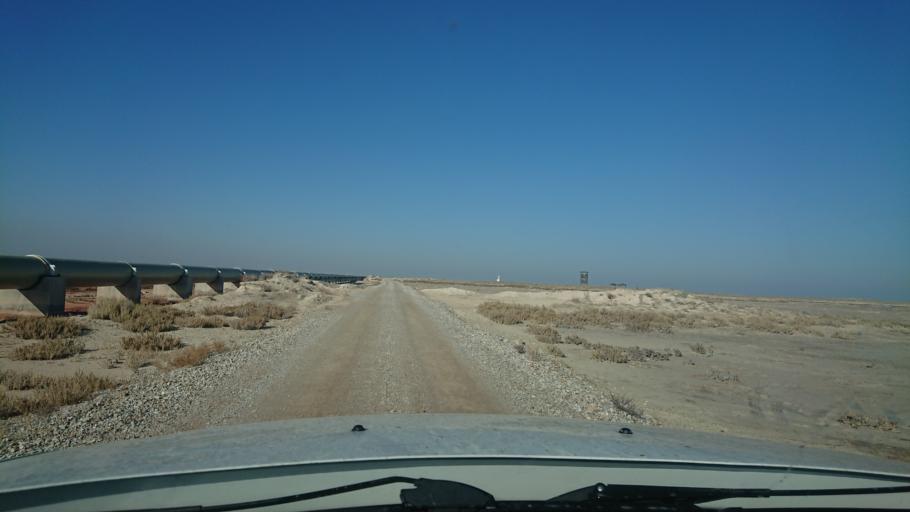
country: TR
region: Aksaray
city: Eskil
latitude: 38.4213
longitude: 33.5017
